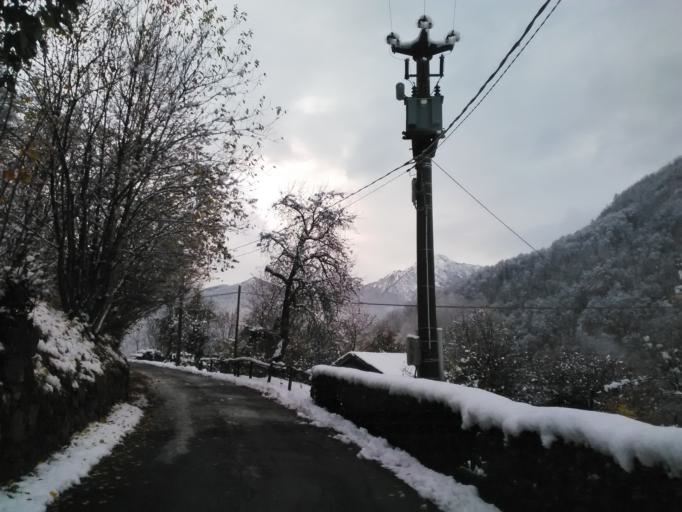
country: IT
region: Piedmont
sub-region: Provincia di Vercelli
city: Varallo
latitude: 45.7920
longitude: 8.2569
